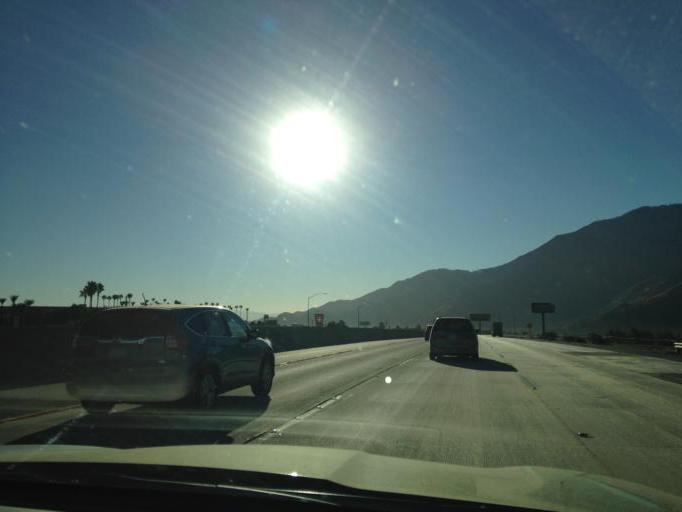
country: US
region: California
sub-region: Riverside County
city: Cabazon
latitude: 33.9210
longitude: -116.8059
